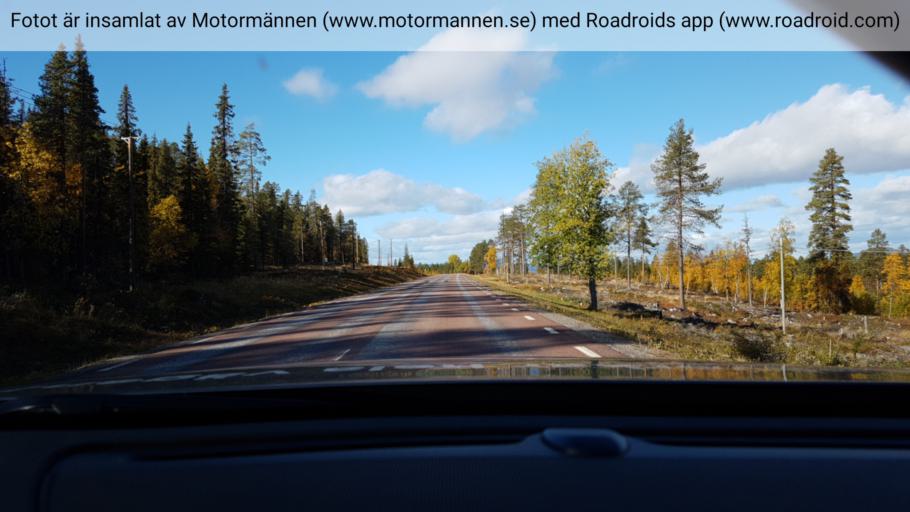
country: SE
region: Norrbotten
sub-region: Arjeplogs Kommun
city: Arjeplog
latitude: 66.0589
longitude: 17.9682
